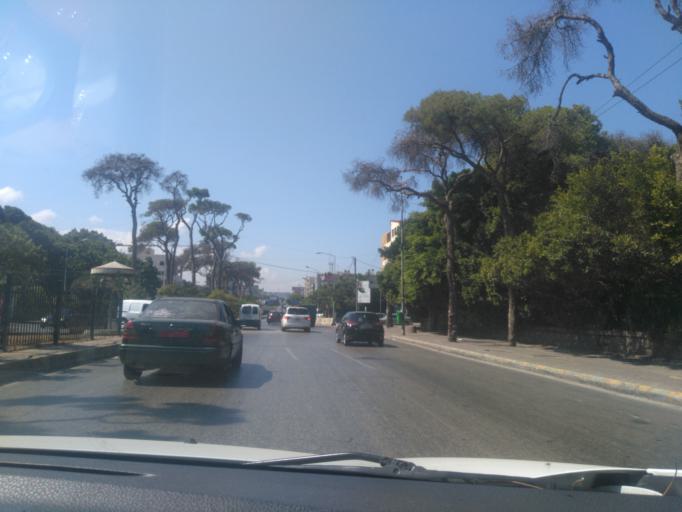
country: LB
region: Beyrouth
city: Beirut
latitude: 33.8538
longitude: 35.5013
